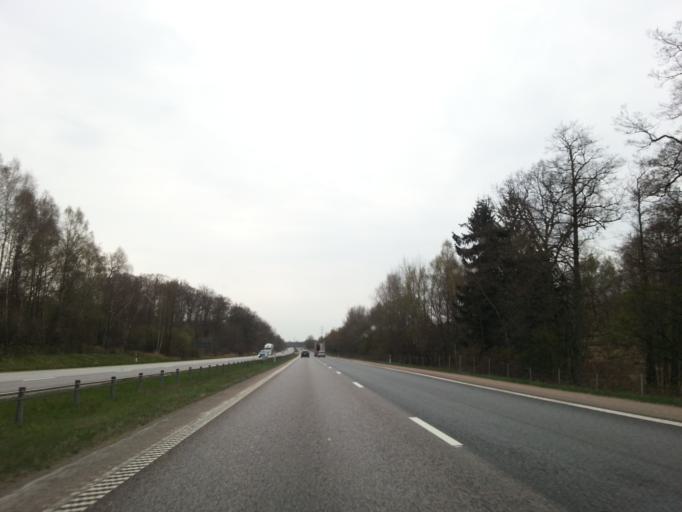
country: SE
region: Halland
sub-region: Halmstads Kommun
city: Halmstad
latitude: 56.7066
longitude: 12.8900
